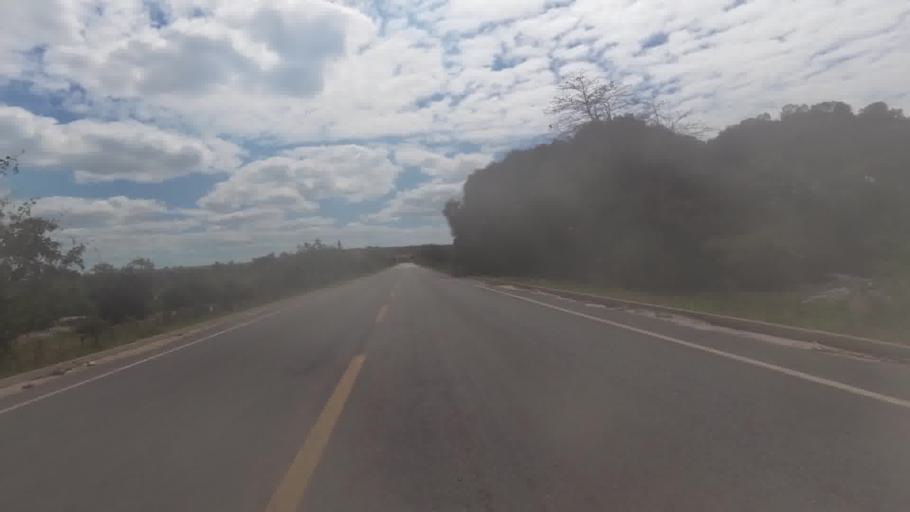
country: BR
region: Espirito Santo
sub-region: Marataizes
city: Marataizes
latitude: -21.2077
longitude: -40.9658
